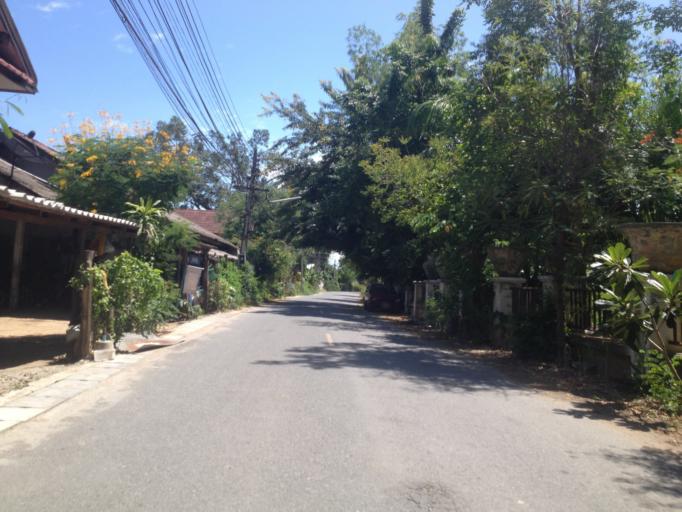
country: TH
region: Chiang Mai
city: Hang Dong
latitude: 18.6804
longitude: 98.9284
